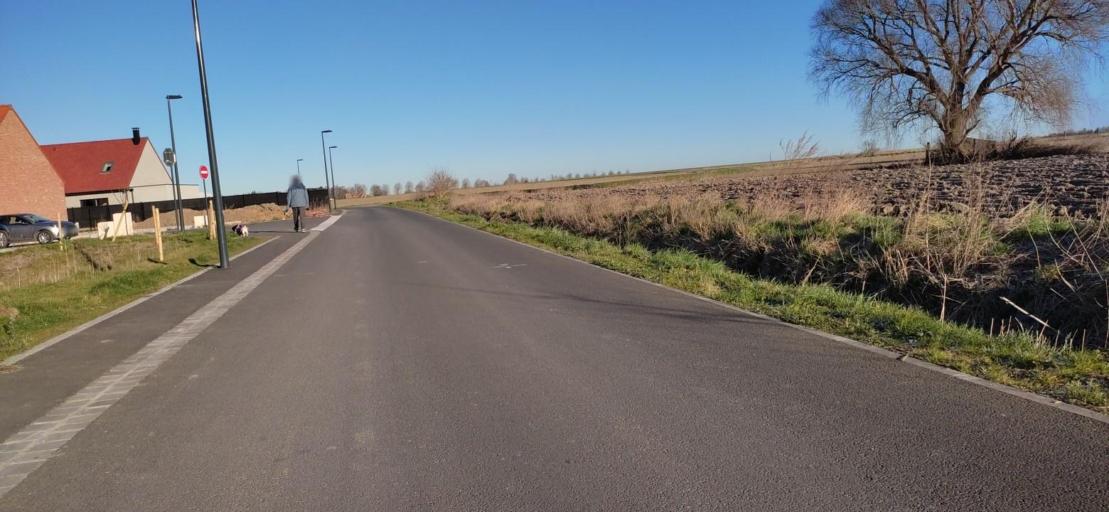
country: FR
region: Nord-Pas-de-Calais
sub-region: Departement du Nord
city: Camphin-en-Carembault
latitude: 50.4983
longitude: 2.9766
